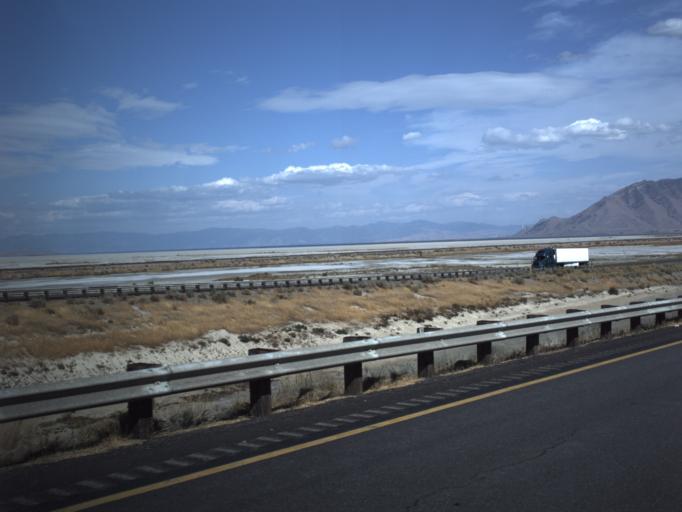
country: US
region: Utah
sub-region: Tooele County
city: Grantsville
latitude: 40.6833
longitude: -112.4380
